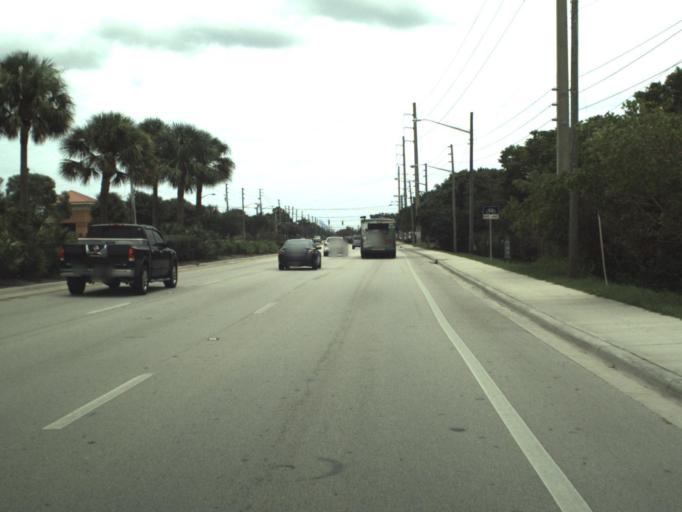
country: US
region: Florida
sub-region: Palm Beach County
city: Jupiter
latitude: 26.9339
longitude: -80.1128
